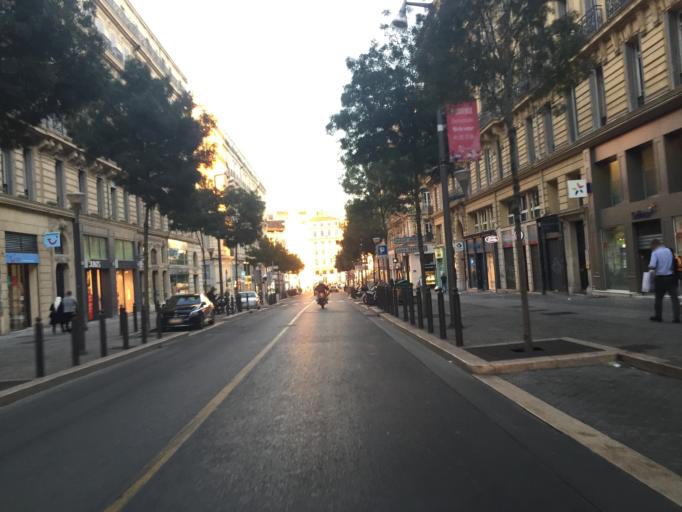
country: FR
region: Provence-Alpes-Cote d'Azur
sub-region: Departement des Bouches-du-Rhone
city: Marseille 02
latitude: 43.2975
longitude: 5.3731
